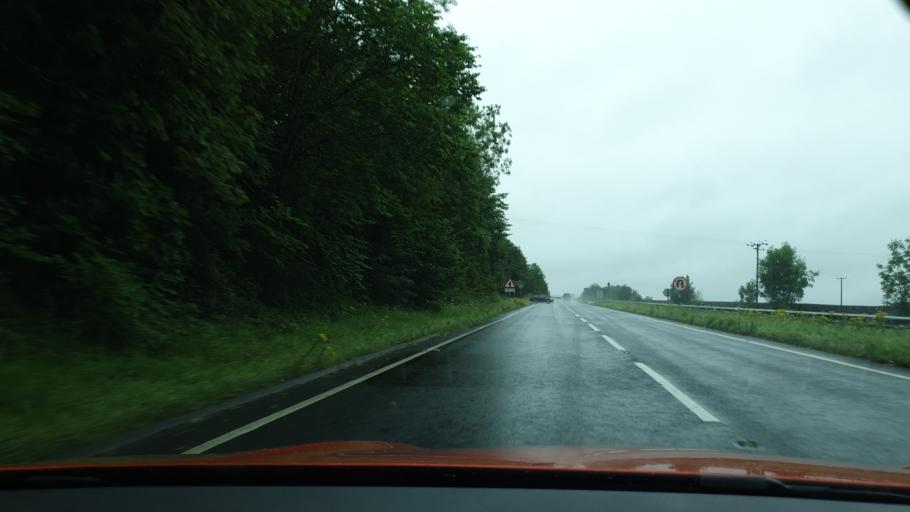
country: GB
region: England
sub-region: Cumbria
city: Grange-over-Sands
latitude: 54.2215
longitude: -2.9040
